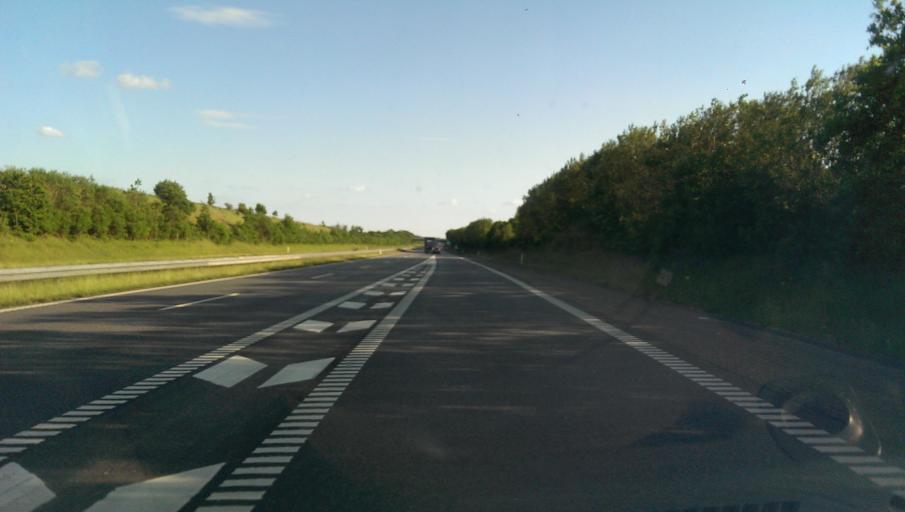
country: DK
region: South Denmark
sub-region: Esbjerg Kommune
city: Esbjerg
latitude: 55.5067
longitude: 8.5026
